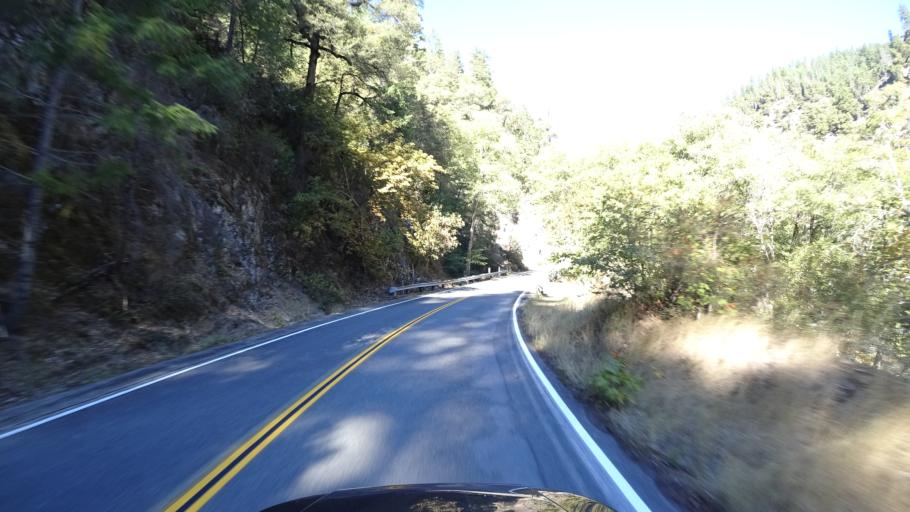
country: US
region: California
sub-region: Siskiyou County
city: Happy Camp
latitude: 41.3478
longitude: -123.4067
